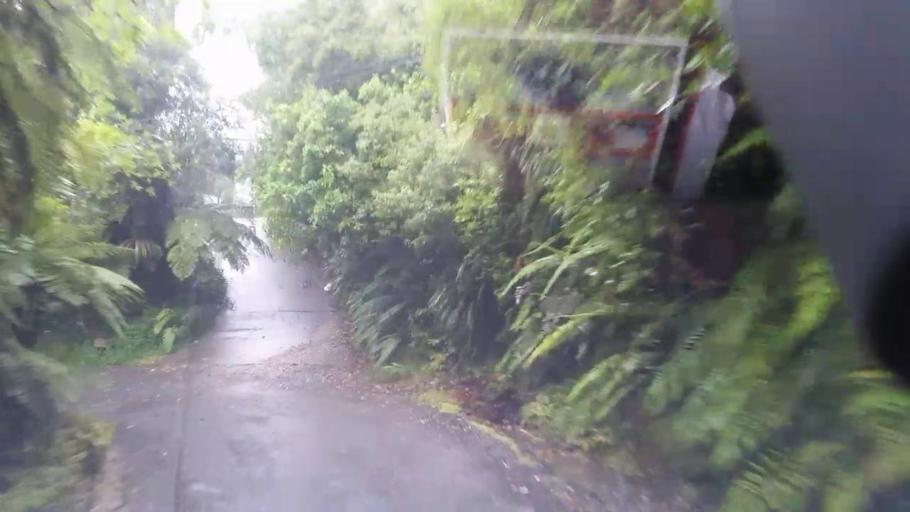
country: NZ
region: Auckland
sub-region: Auckland
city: Titirangi
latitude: -36.9203
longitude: 174.5627
